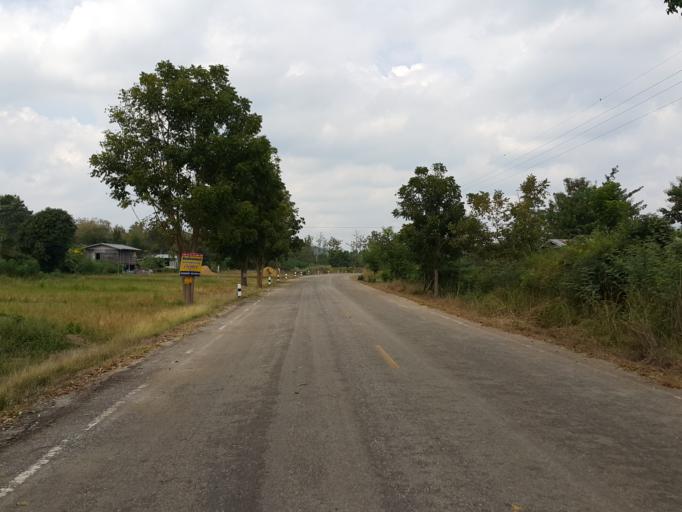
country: TH
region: Sukhothai
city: Thung Saliam
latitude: 17.3795
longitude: 99.5871
